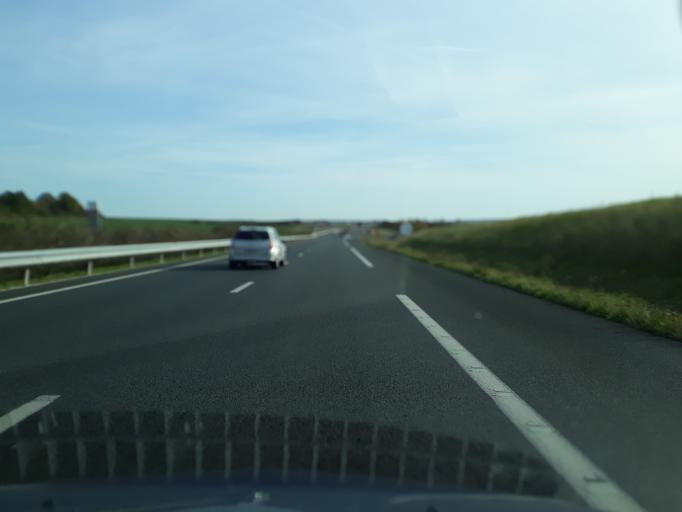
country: FR
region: Bourgogne
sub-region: Departement de l'Yonne
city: Thorigny-sur-Oreuse
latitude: 48.2449
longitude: 3.5581
